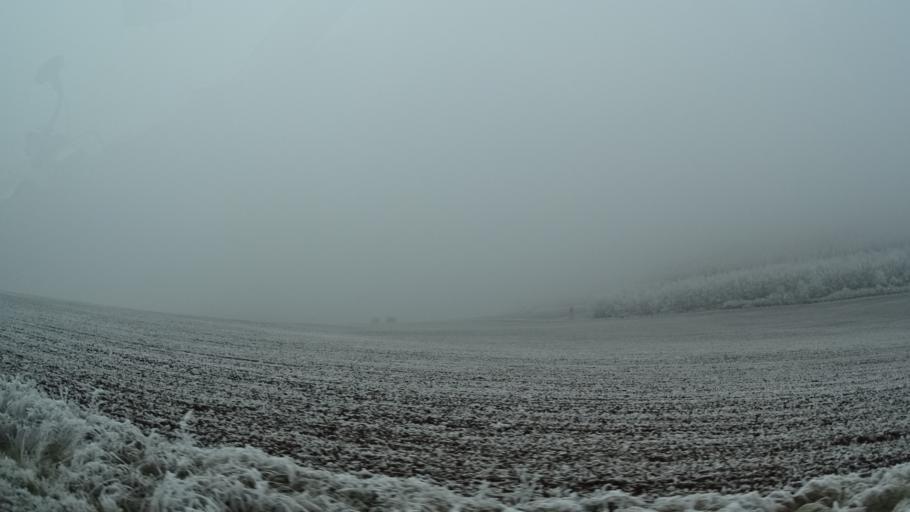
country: DE
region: Thuringia
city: Henneberg
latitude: 50.5194
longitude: 10.3300
